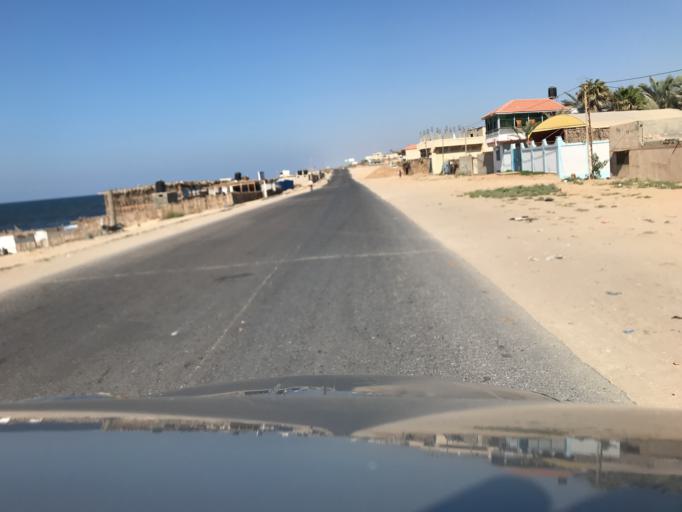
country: PS
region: Gaza Strip
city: Dayr al Balah
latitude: 31.4327
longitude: 34.3458
